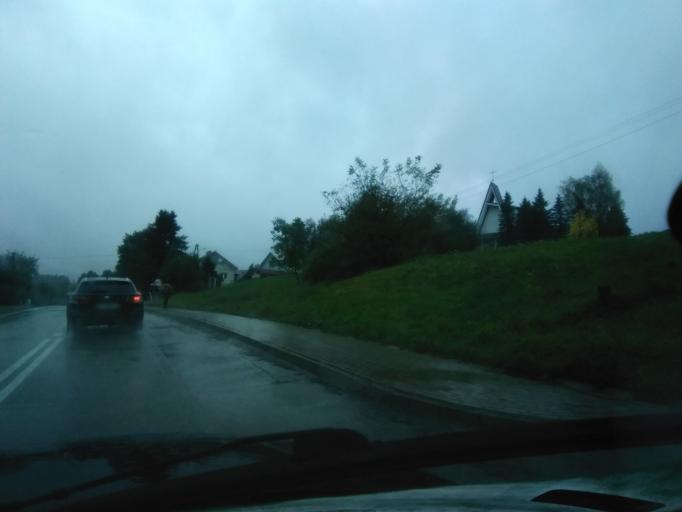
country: PL
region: Subcarpathian Voivodeship
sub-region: Powiat ropczycko-sedziszowski
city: Wielopole Skrzynskie
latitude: 49.9695
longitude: 21.5807
